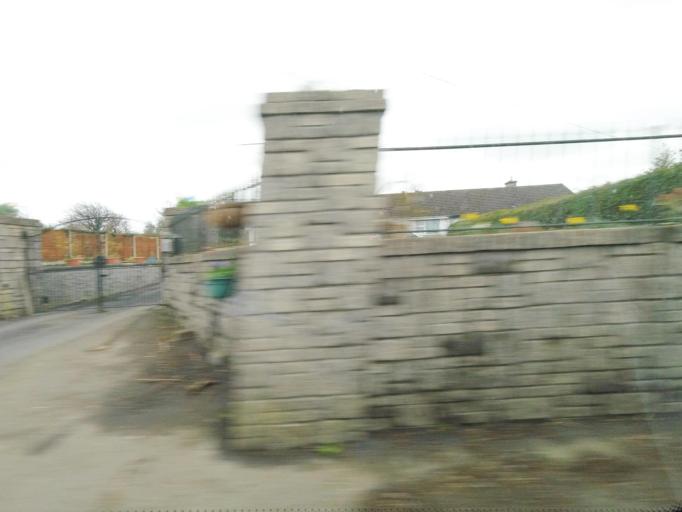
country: IE
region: Leinster
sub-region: Kildare
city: Naas
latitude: 53.1764
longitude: -6.6751
